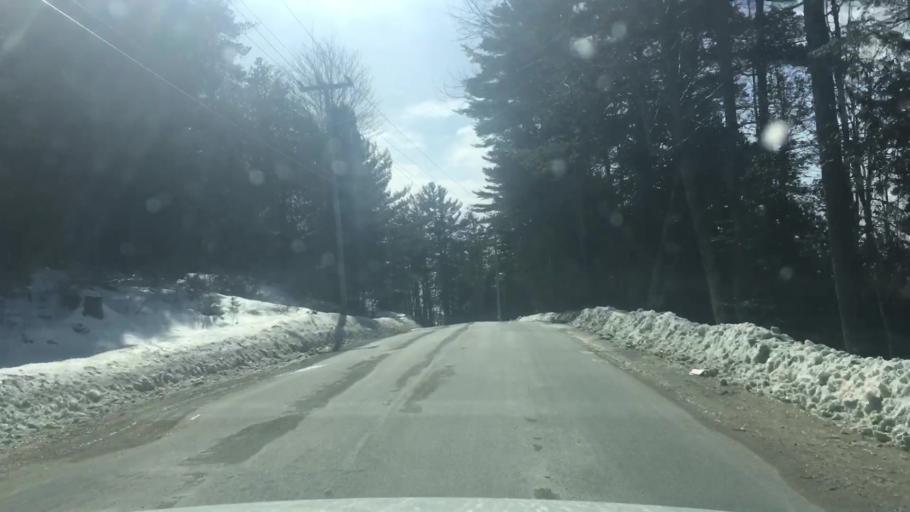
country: US
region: Maine
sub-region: Penobscot County
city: Holden
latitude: 44.7497
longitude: -68.6326
